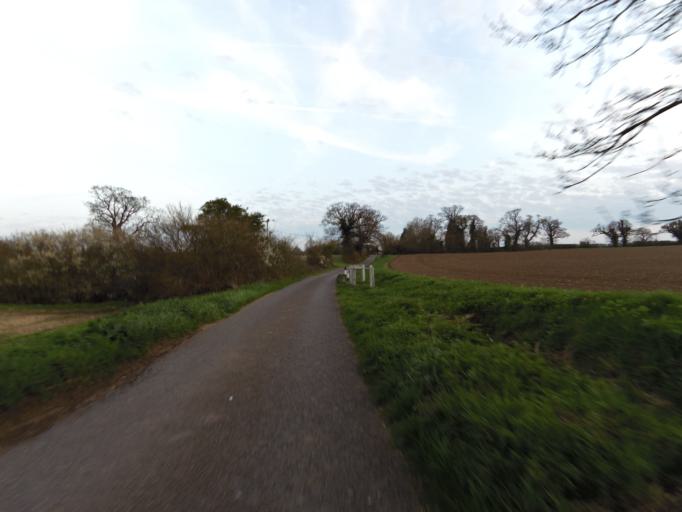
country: GB
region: England
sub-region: Suffolk
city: Kesgrave
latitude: 52.1103
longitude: 1.2342
